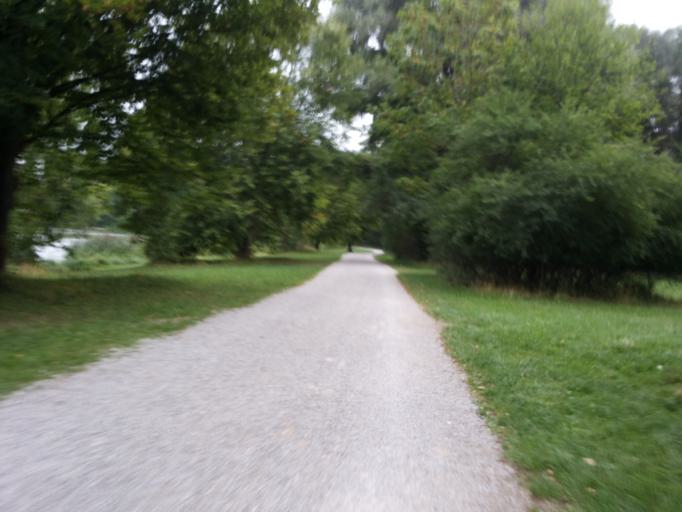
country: DE
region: Bavaria
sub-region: Upper Bavaria
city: Ingolstadt
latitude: 48.7485
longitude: 11.4011
